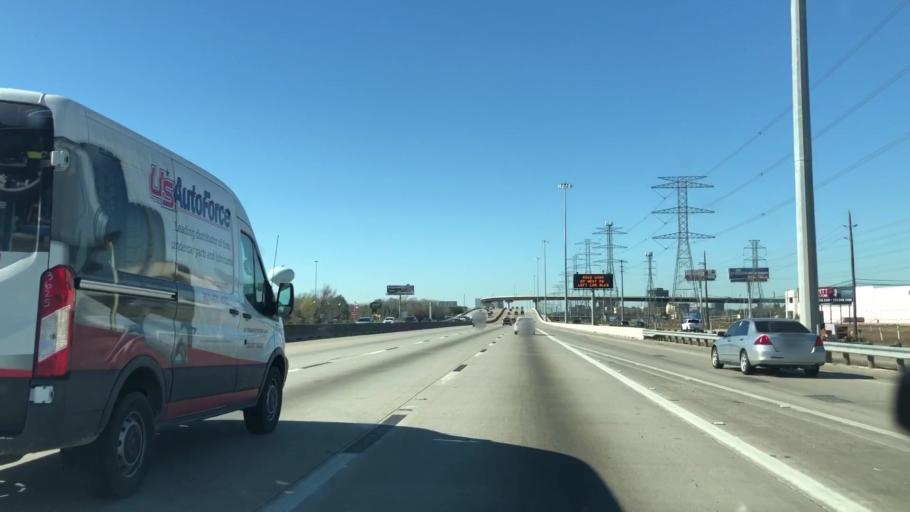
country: US
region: Texas
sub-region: Harris County
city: Aldine
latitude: 29.9375
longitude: -95.3767
